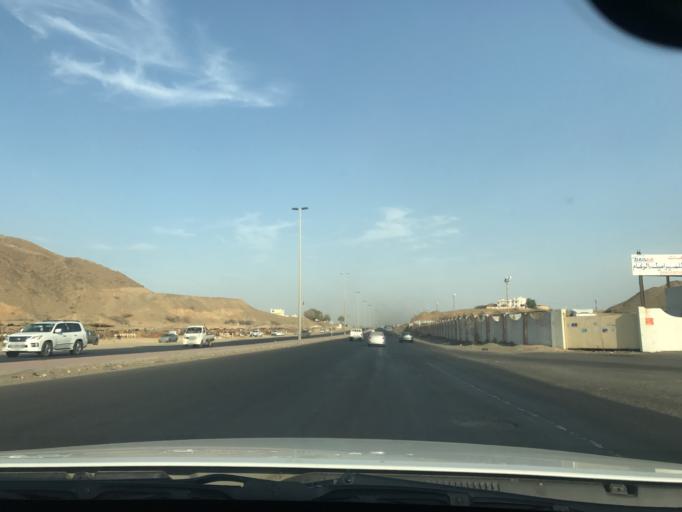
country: SA
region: Makkah
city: Jeddah
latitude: 21.4155
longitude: 39.4145
